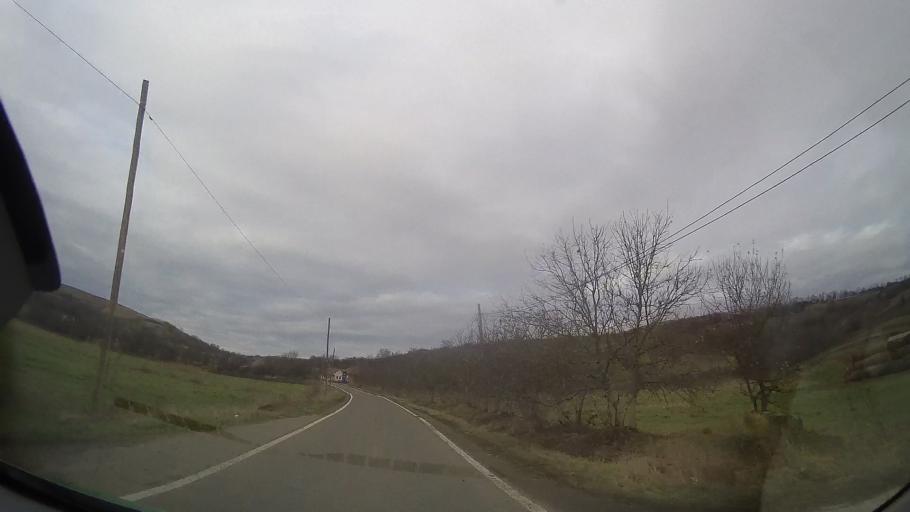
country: RO
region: Mures
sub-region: Comuna Cozma
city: Cozma
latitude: 46.8024
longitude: 24.5340
